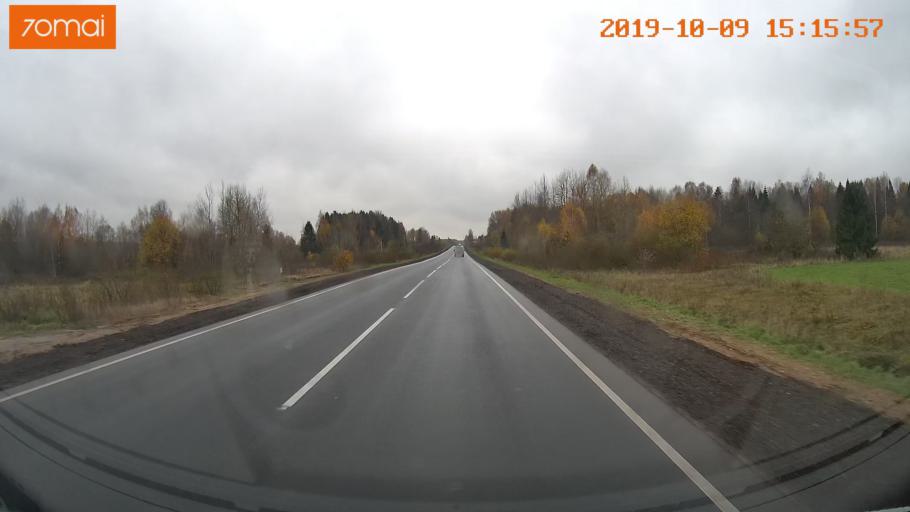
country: RU
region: Kostroma
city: Susanino
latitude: 58.1160
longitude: 41.5877
